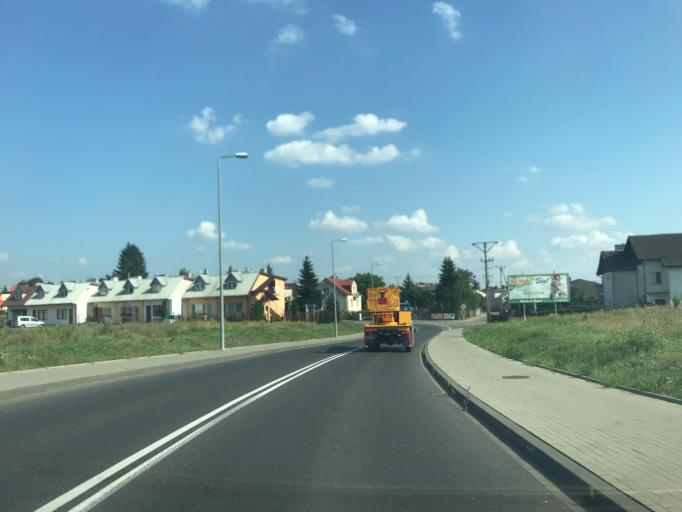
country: PL
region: Masovian Voivodeship
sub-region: Powiat mlawski
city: Mlawa
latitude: 53.1084
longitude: 20.3670
